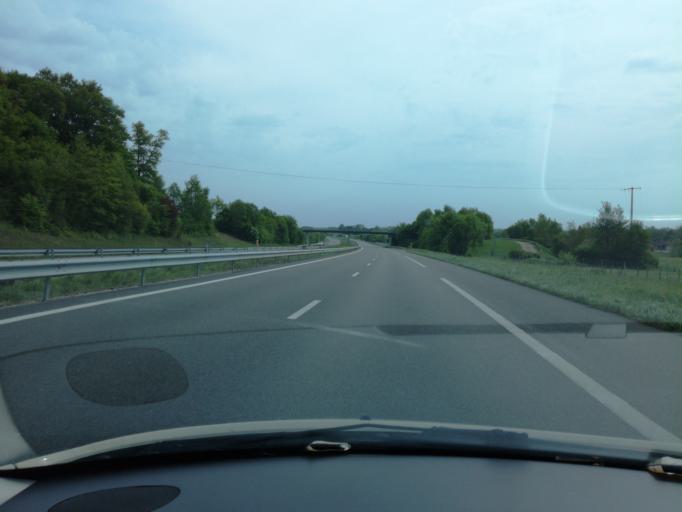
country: FR
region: Rhone-Alpes
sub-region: Departement de l'Ain
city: Marboz
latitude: 46.3854
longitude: 5.2704
